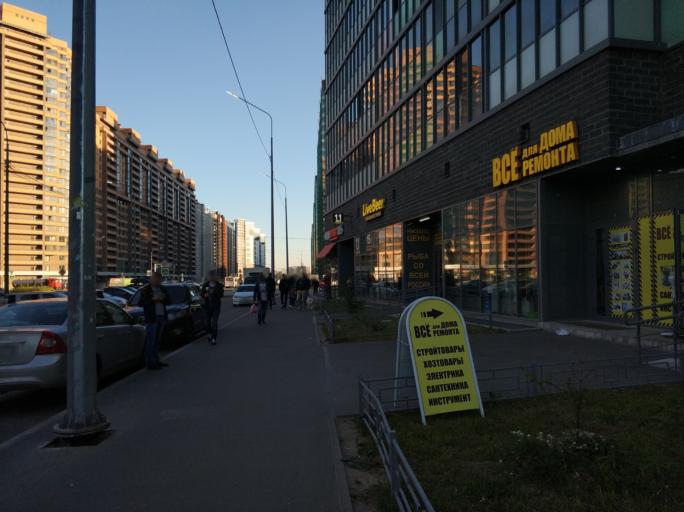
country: RU
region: Leningrad
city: Murino
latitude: 60.0588
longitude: 30.4294
